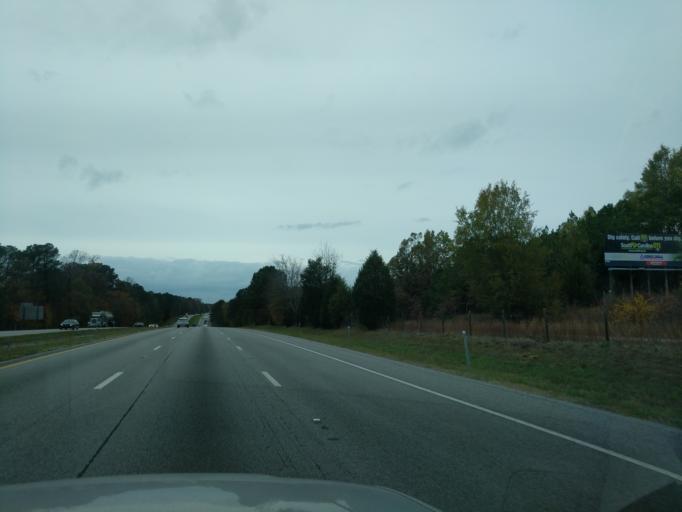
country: US
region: South Carolina
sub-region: Laurens County
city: Joanna
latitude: 34.4410
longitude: -81.7635
